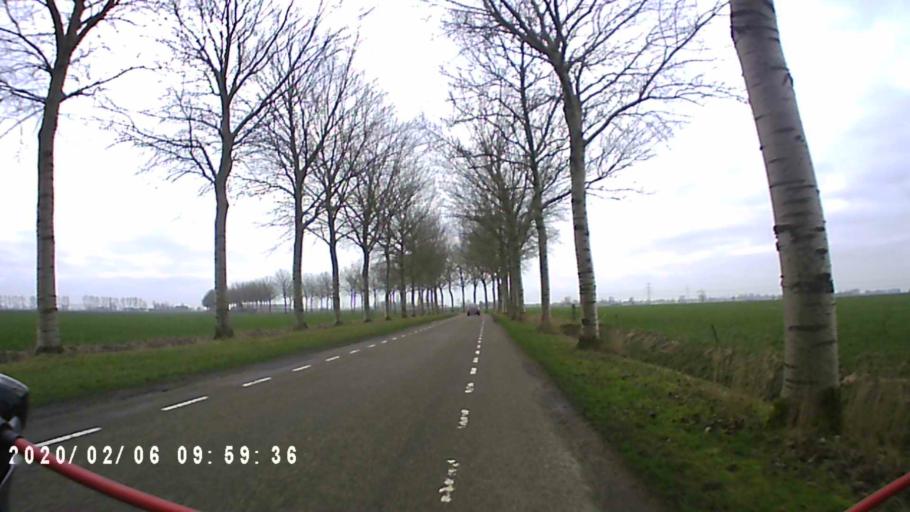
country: NL
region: Groningen
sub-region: Gemeente Zuidhorn
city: Aduard
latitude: 53.2681
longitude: 6.4929
